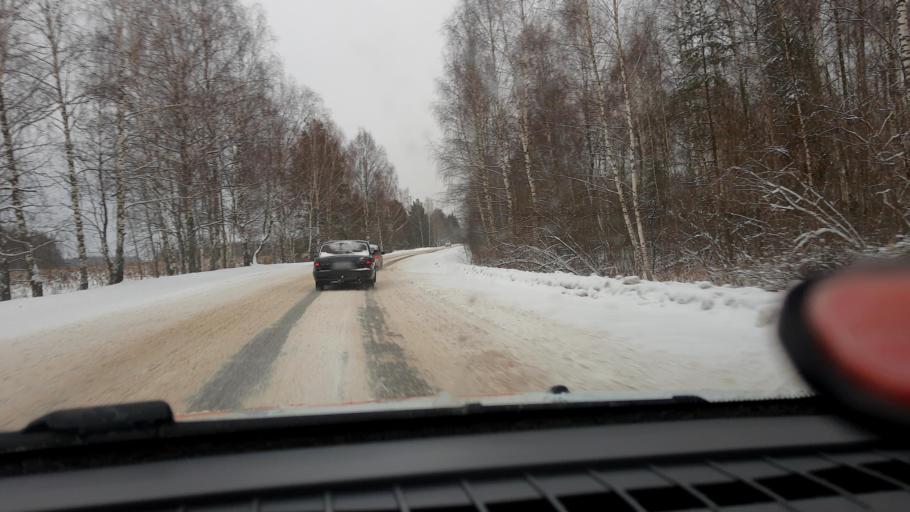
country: RU
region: Nizjnij Novgorod
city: Pamyat' Parizhskoy Kommuny
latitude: 56.2650
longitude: 44.4389
